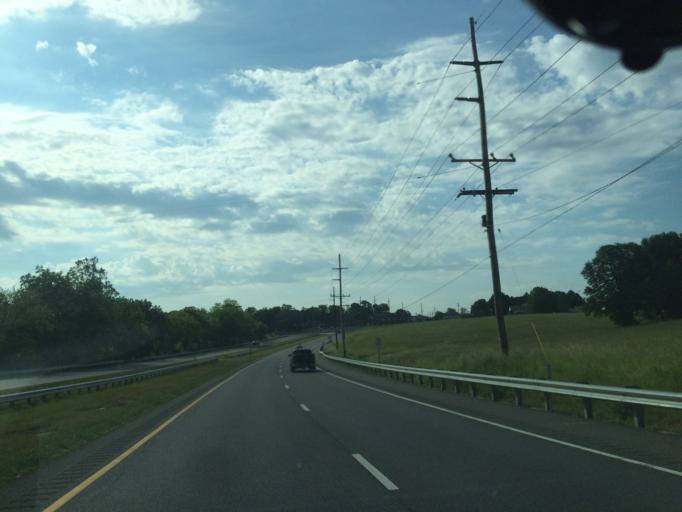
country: US
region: Maryland
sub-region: Carroll County
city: Westminster
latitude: 39.5460
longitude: -76.9383
